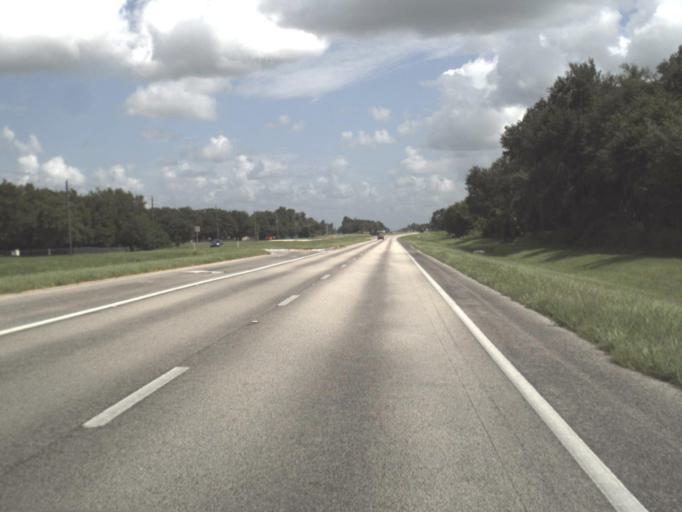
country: US
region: Florida
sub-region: DeSoto County
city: Arcadia
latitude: 27.2522
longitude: -81.8442
